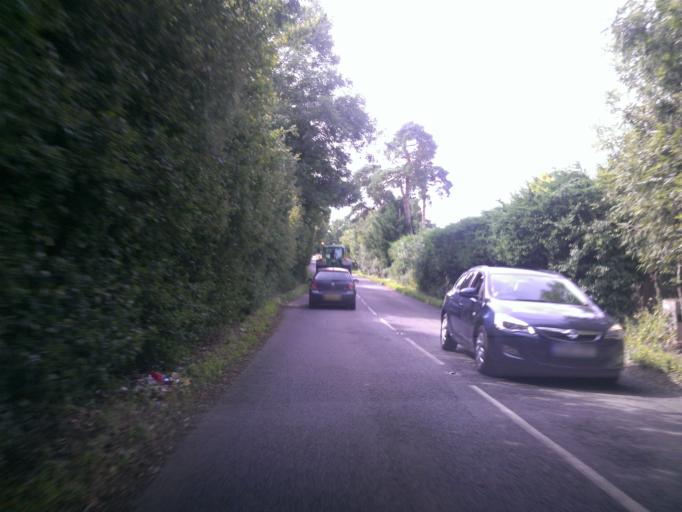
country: GB
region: England
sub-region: Kent
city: Tonbridge
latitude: 51.2035
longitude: 0.2202
